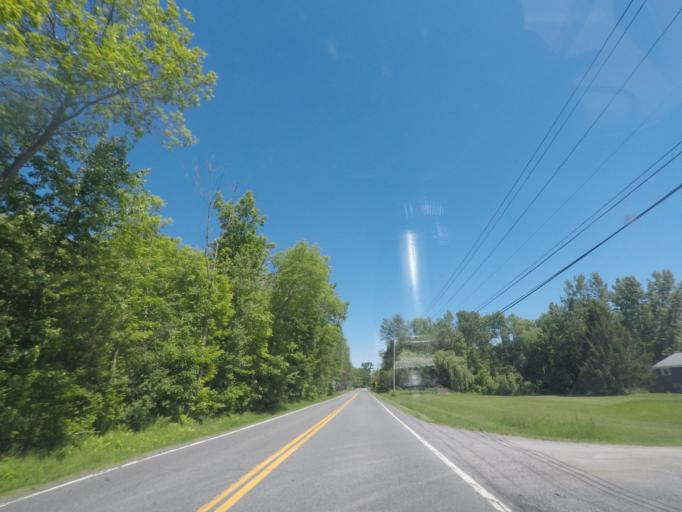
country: US
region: New York
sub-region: Schenectady County
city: East Glenville
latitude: 42.8798
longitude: -73.8650
